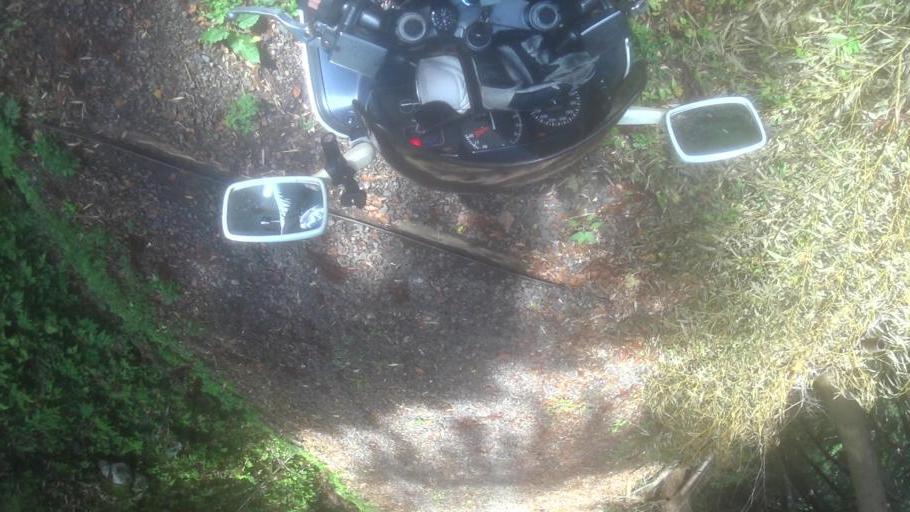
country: JP
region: Kyoto
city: Miyazu
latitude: 35.6243
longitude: 135.1611
